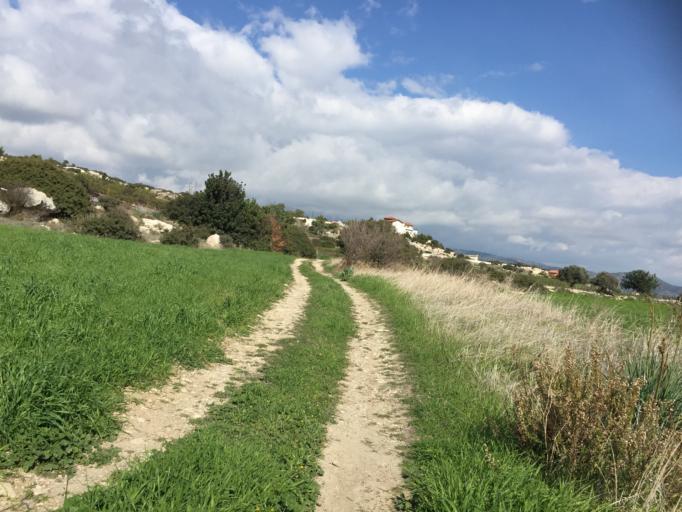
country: CY
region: Larnaka
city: Agios Tychon
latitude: 34.7414
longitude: 33.1410
